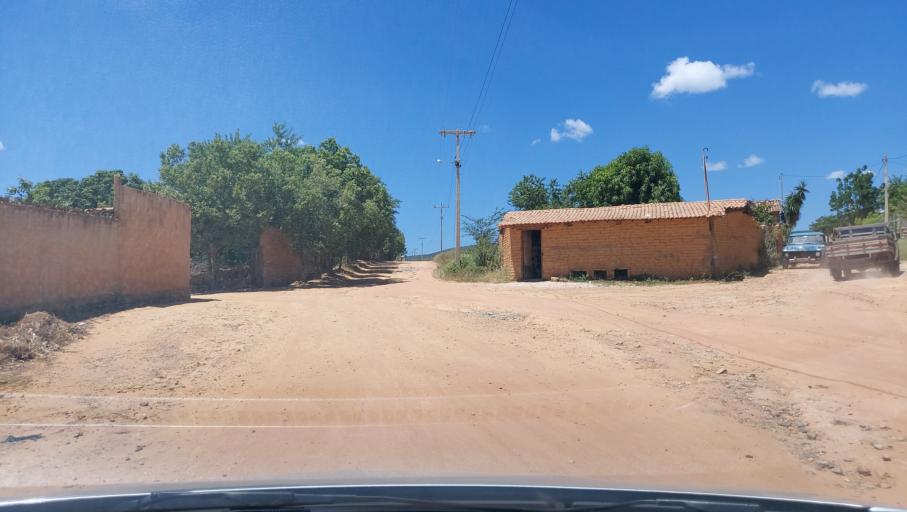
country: BR
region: Bahia
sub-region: Oliveira Dos Brejinhos
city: Beira Rio
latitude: -12.0024
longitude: -42.6297
